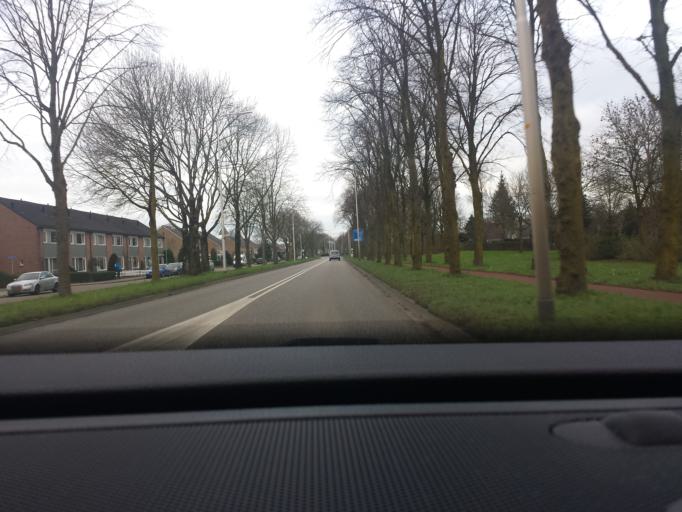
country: NL
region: Gelderland
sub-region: Gemeente Zevenaar
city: Zevenaar
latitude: 51.9276
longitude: 6.0897
